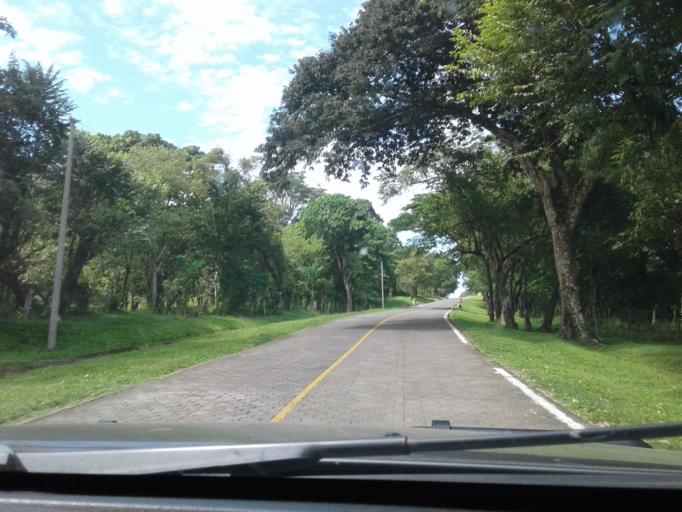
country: NI
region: Rivas
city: Cardenas
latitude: 11.1738
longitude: -85.4834
